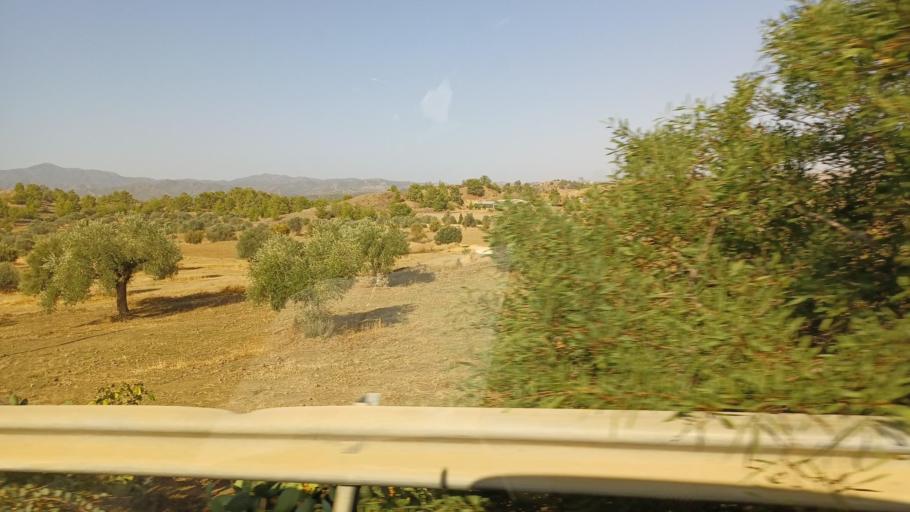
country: CY
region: Lefkosia
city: Alampra
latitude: 34.9799
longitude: 33.3461
